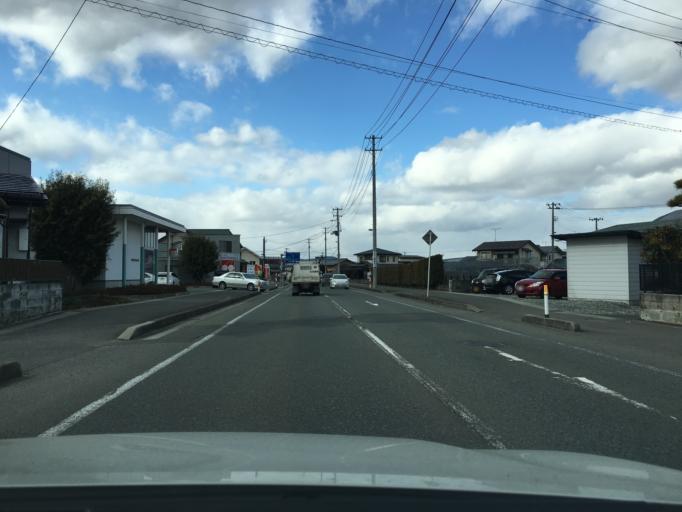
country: JP
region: Yamagata
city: Kaminoyama
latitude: 38.2060
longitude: 140.3083
